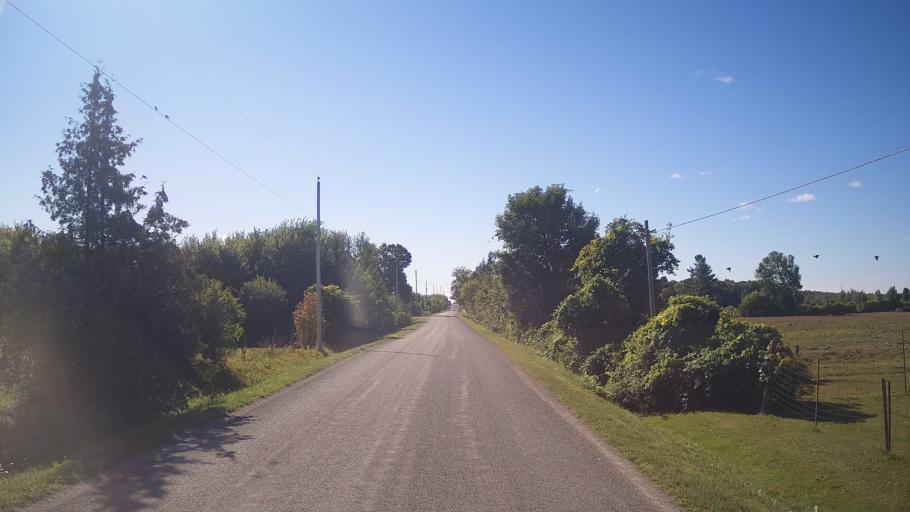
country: CA
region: Ontario
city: Prescott
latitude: 44.9795
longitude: -75.5762
